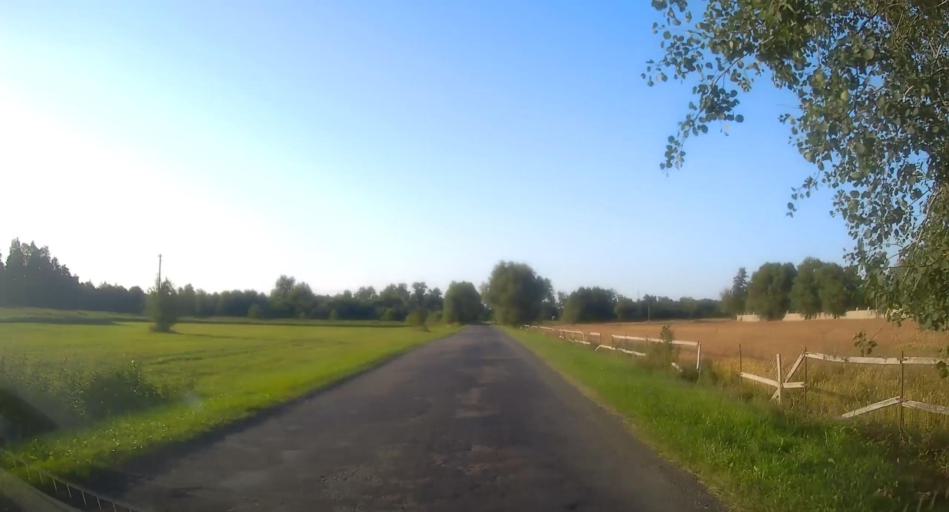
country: PL
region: Lodz Voivodeship
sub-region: Powiat skierniewicki
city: Kaweczyn Nowy
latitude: 51.8976
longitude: 20.2984
